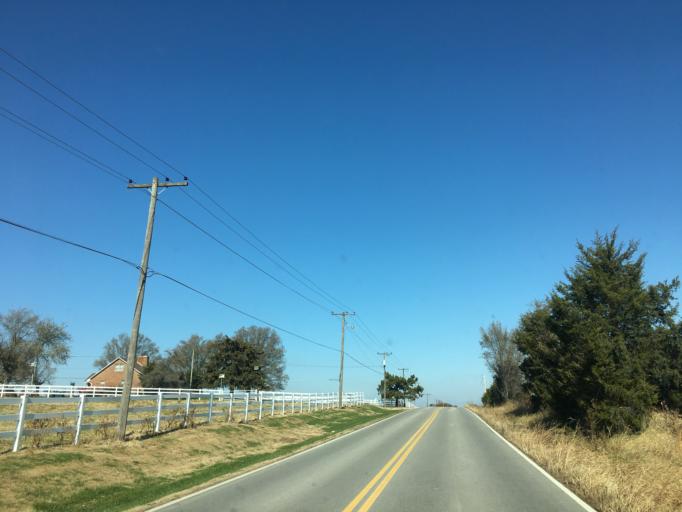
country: US
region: Missouri
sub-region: Cole County
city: Wardsville
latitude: 38.5027
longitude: -92.1760
